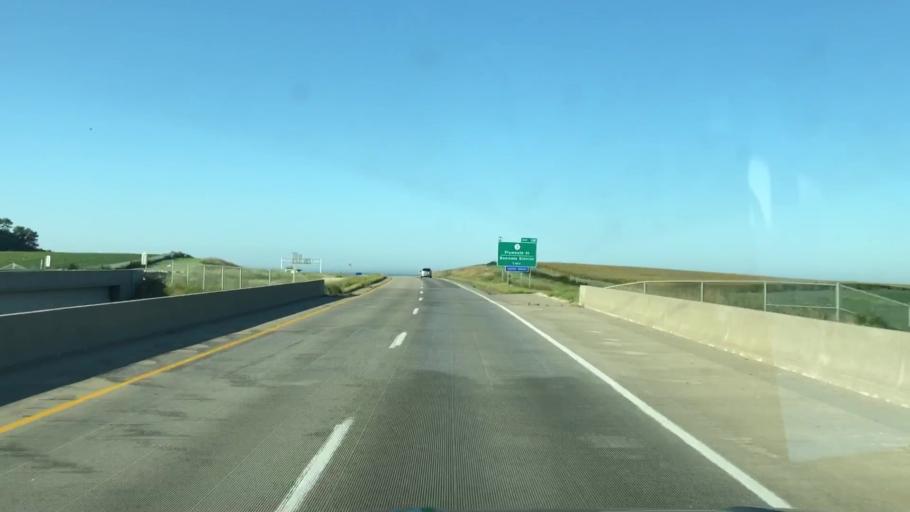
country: US
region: Iowa
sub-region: Plymouth County
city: Le Mars
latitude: 42.8122
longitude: -96.1941
